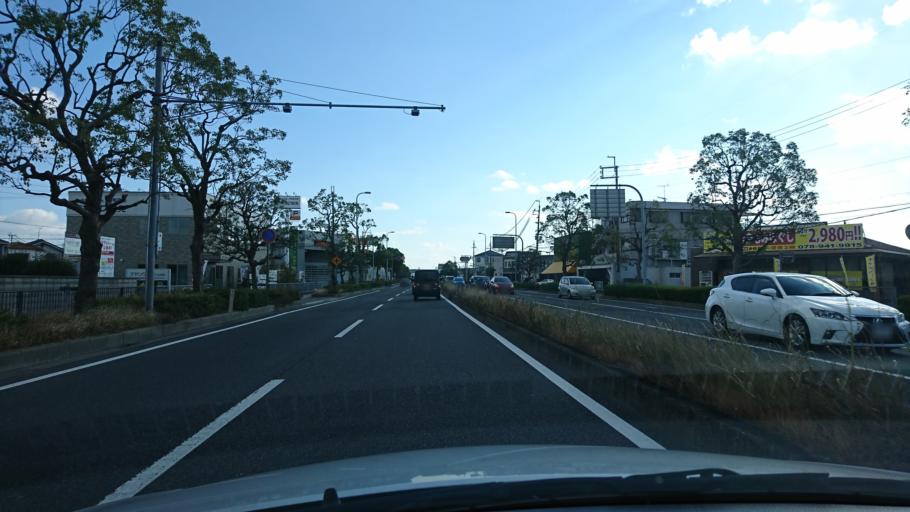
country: JP
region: Hyogo
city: Kakogawacho-honmachi
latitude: 34.7164
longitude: 134.8765
